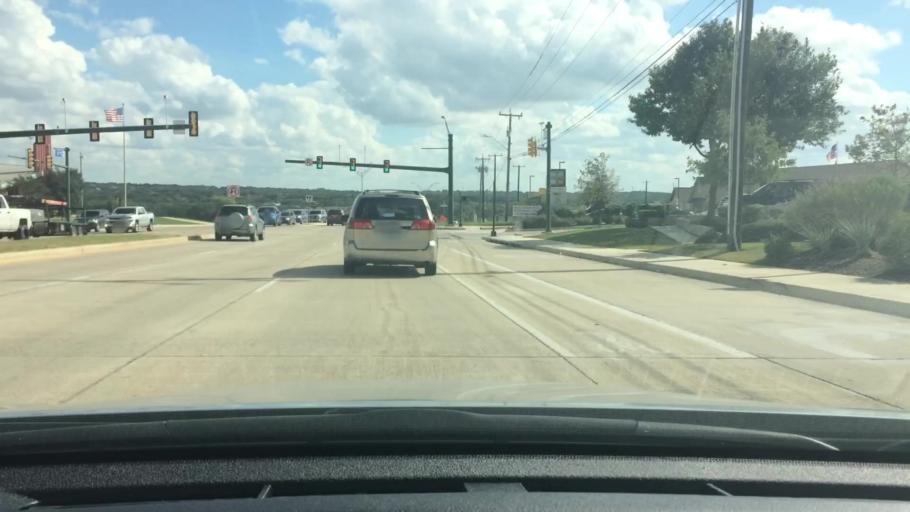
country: US
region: Texas
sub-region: Bexar County
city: Hollywood Park
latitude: 29.6082
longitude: -98.4192
